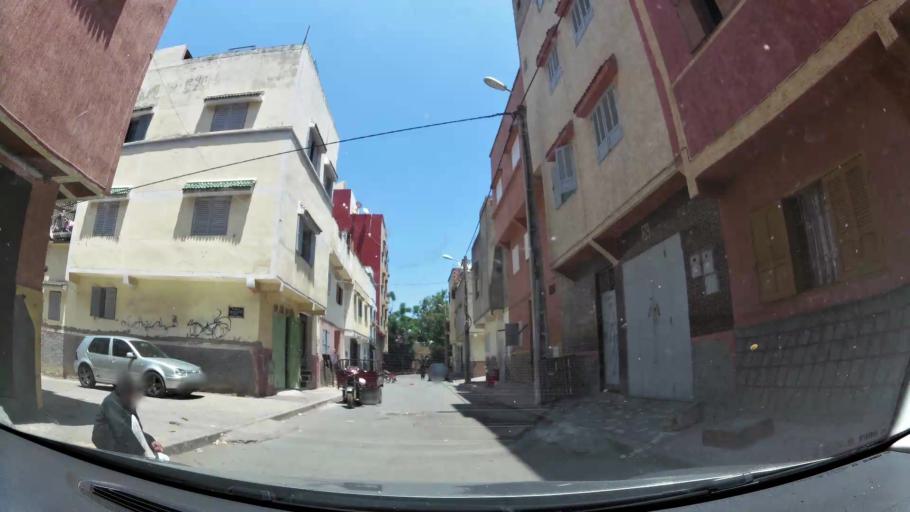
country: MA
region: Rabat-Sale-Zemmour-Zaer
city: Sale
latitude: 34.0602
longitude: -6.7939
